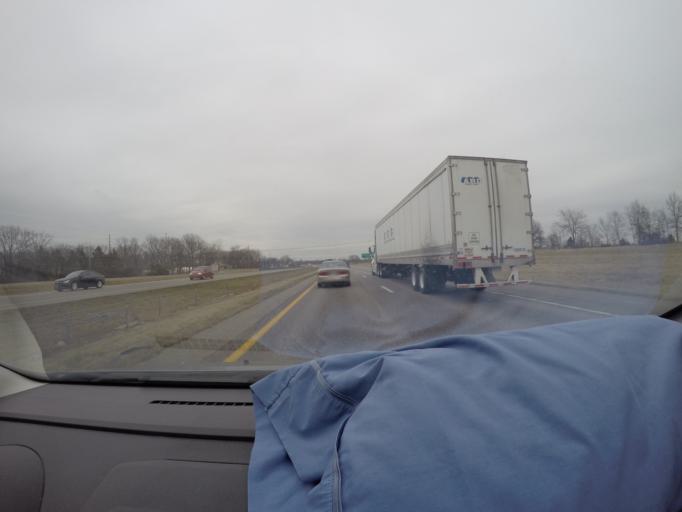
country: US
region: Missouri
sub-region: Saint Charles County
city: Wentzville
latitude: 38.8051
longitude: -90.9073
